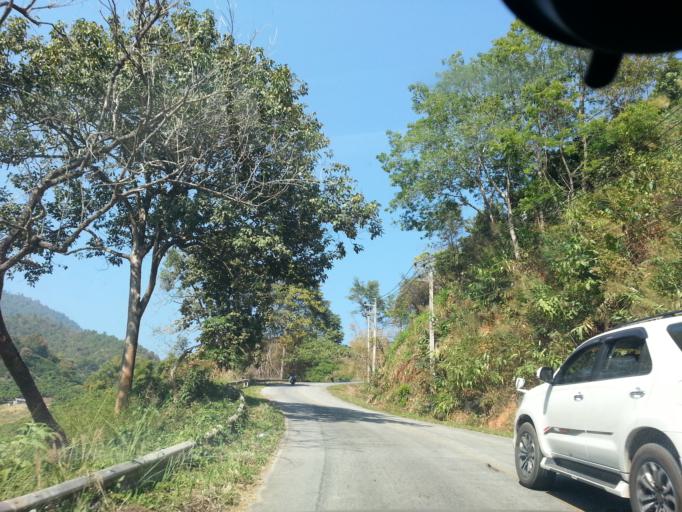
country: TH
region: Chiang Mai
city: Chai Prakan
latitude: 19.8252
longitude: 99.0988
